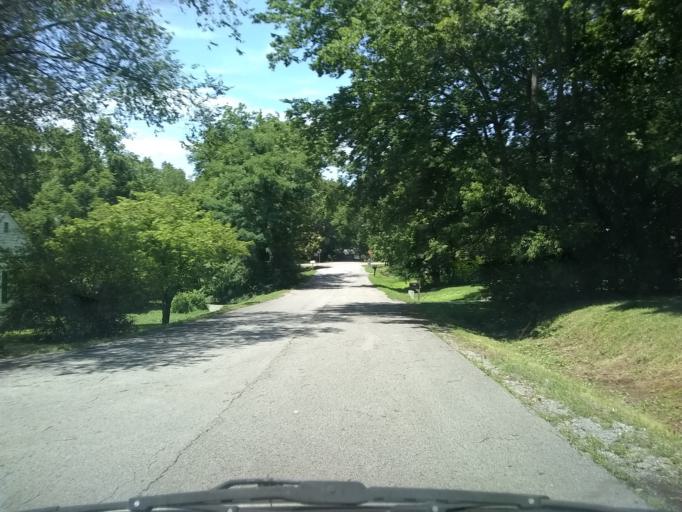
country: US
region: Tennessee
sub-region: Davidson County
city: Nashville
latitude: 36.1293
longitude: -86.7018
